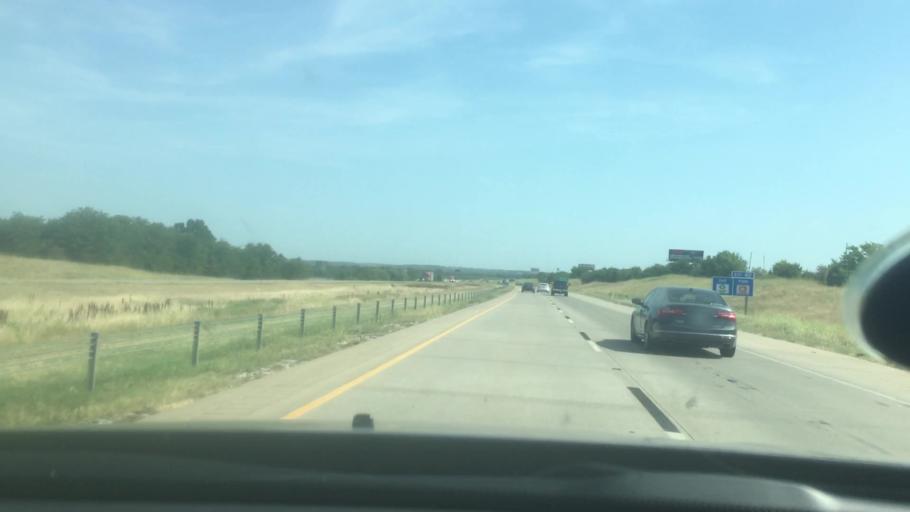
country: US
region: Oklahoma
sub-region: Carter County
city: Ardmore
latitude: 34.2897
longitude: -97.1592
